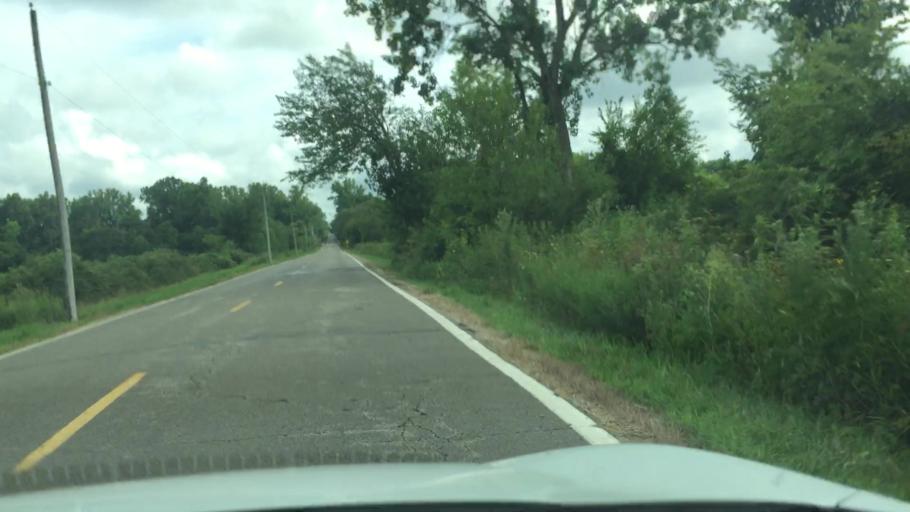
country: US
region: Ohio
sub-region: Clark County
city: Northridge
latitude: 40.0105
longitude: -83.6930
